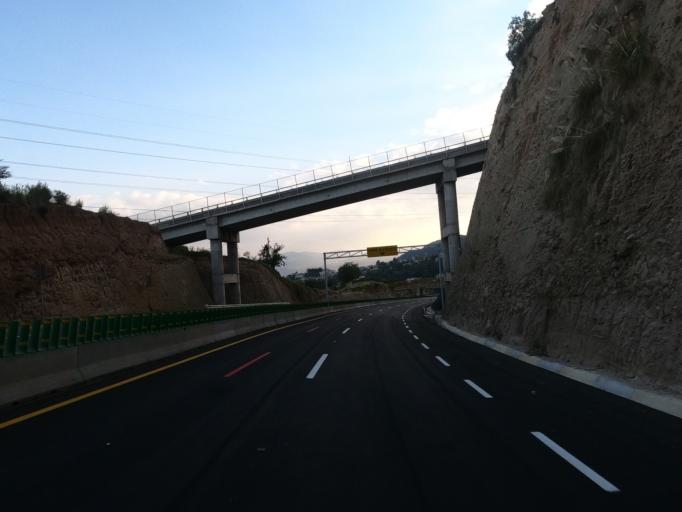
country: MX
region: Mexico
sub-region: Naucalpan de Juarez
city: Llano de las Flores (Barrio del Hueso)
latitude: 19.4312
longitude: -99.3311
